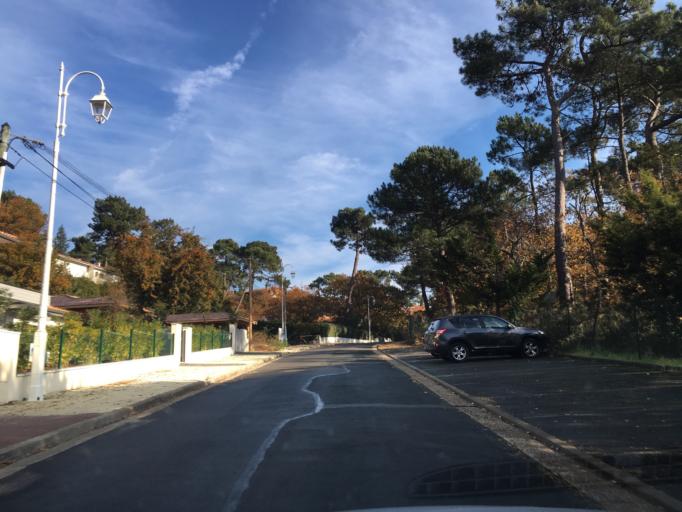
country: FR
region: Aquitaine
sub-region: Departement de la Gironde
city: Arcachon
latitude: 44.6531
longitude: -1.1927
